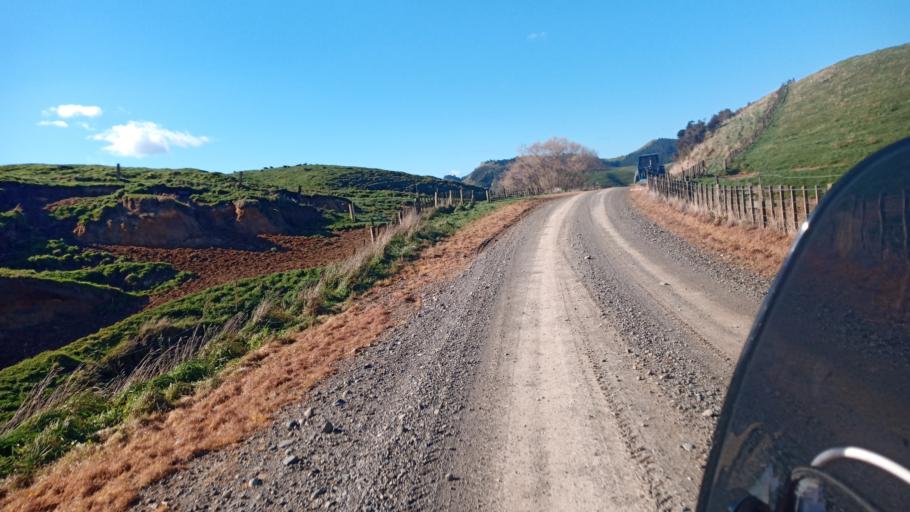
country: NZ
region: Hawke's Bay
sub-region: Wairoa District
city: Wairoa
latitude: -38.7476
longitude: 177.2736
